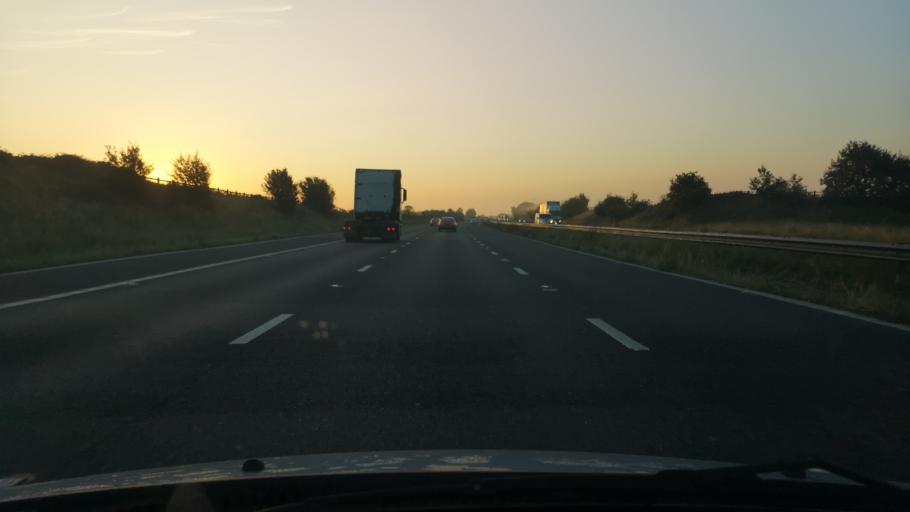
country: GB
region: England
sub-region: East Riding of Yorkshire
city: Pollington
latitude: 53.6922
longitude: -1.1138
